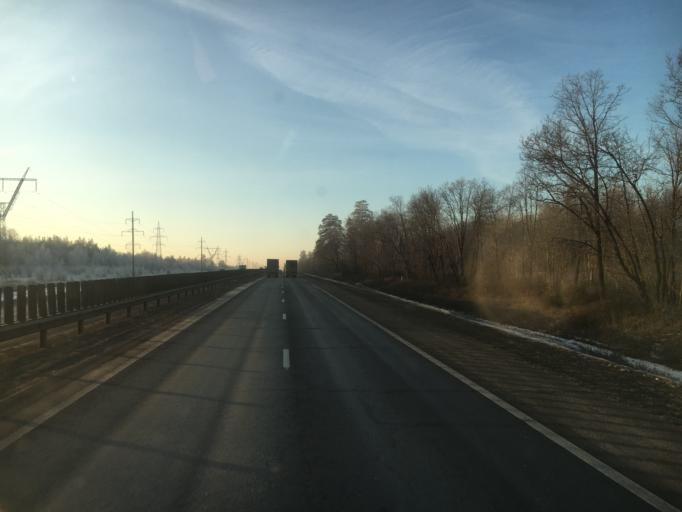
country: RU
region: Samara
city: Pribrezhnyy
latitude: 53.5157
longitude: 49.8693
